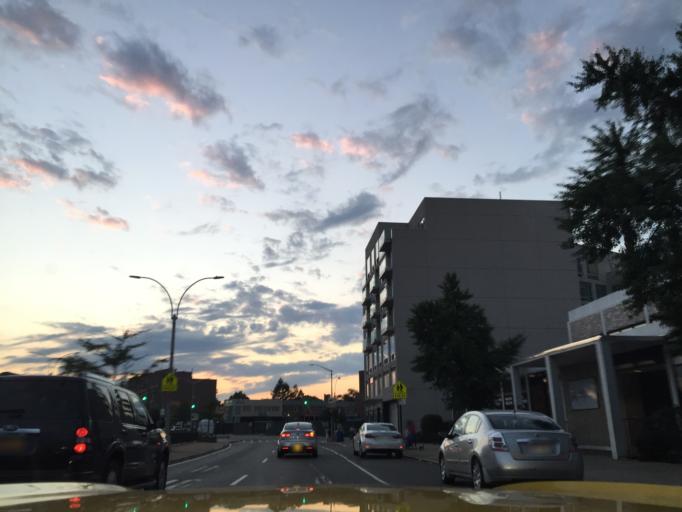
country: US
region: New York
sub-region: Queens County
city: Borough of Queens
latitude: 40.7365
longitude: -73.8767
